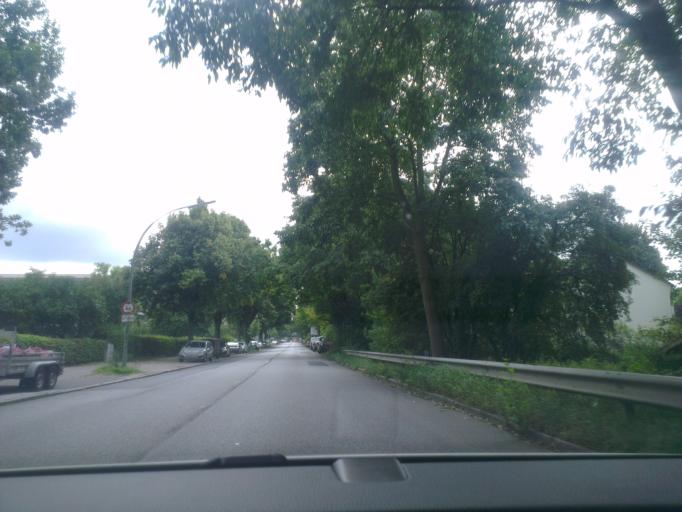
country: DE
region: Hamburg
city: Steilshoop
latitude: 53.5960
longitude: 10.0727
